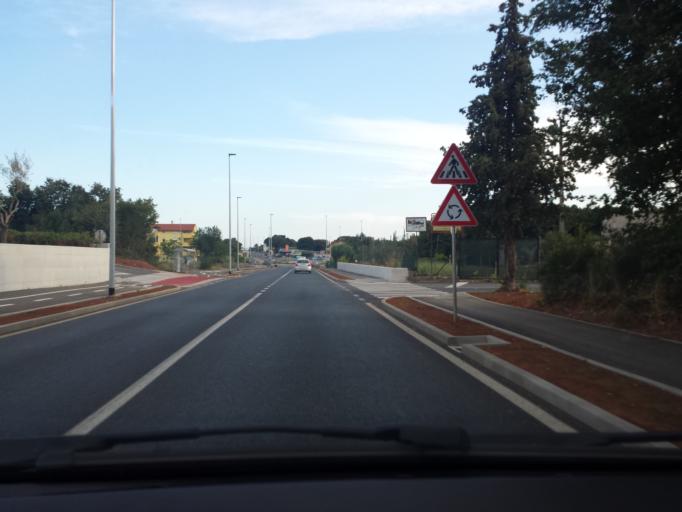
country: HR
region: Istarska
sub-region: Grad Pula
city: Pula
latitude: 44.9006
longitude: 13.8454
